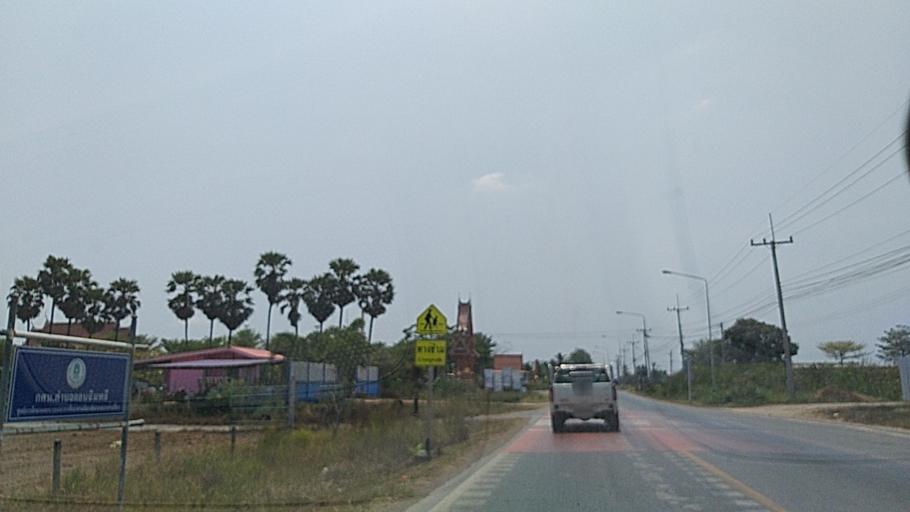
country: TH
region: Chachoengsao
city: Bang Nam Priao
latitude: 13.8642
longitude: 100.9666
